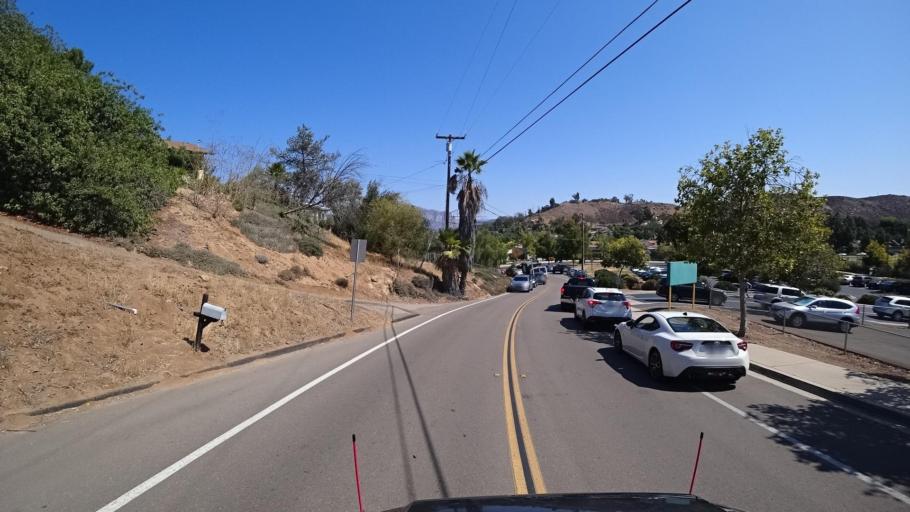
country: US
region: California
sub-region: San Diego County
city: Lakeside
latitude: 32.8517
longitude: -116.9227
